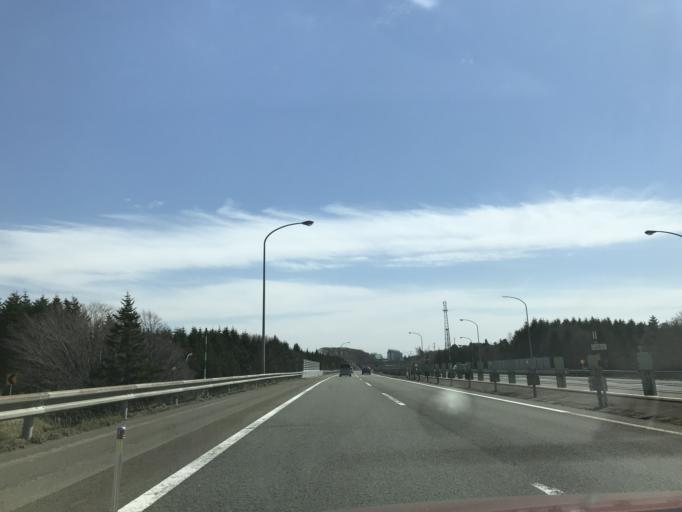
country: JP
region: Hokkaido
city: Ebetsu
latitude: 43.0939
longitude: 141.4953
